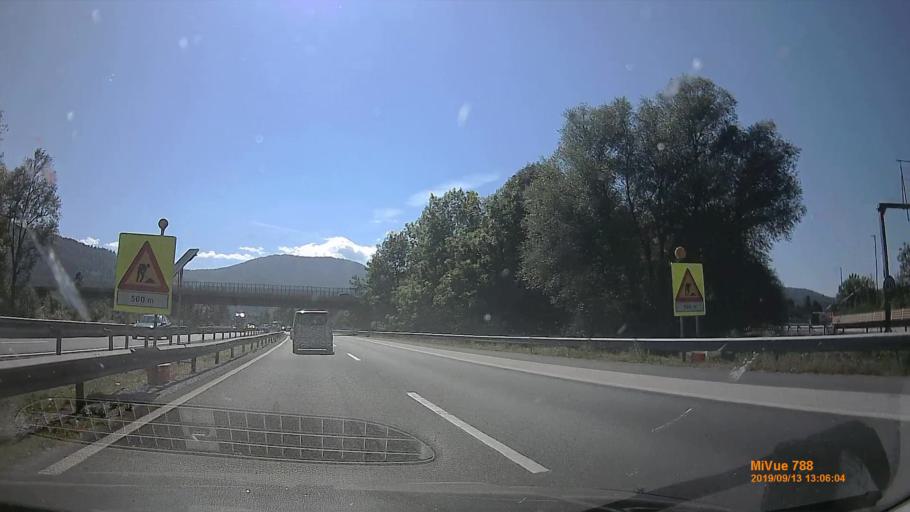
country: SI
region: Vrhnika
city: Vrhnika
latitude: 45.9693
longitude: 14.3050
